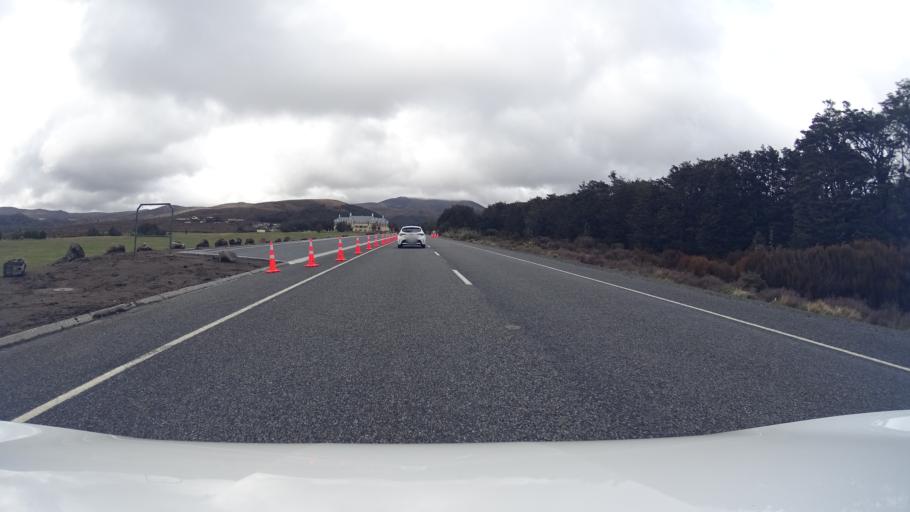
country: NZ
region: Manawatu-Wanganui
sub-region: Ruapehu District
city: Waiouru
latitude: -39.1961
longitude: 175.5363
